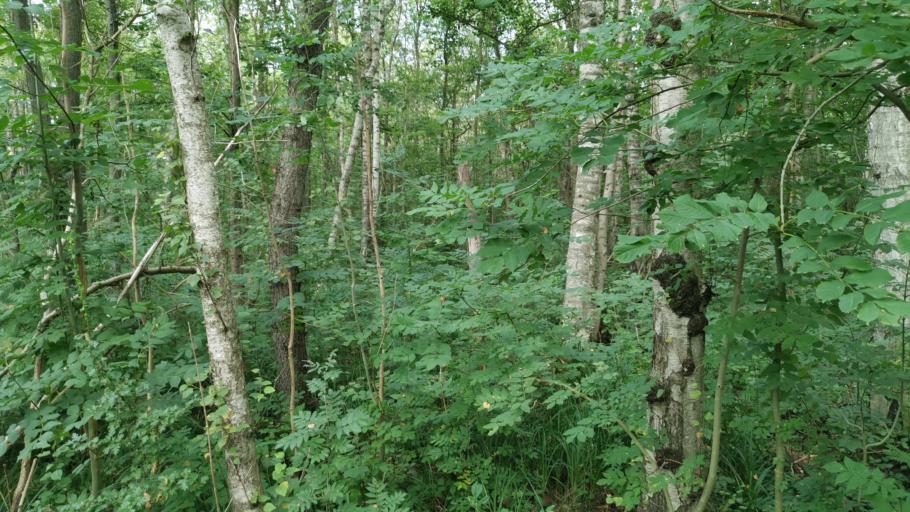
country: DE
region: Mecklenburg-Vorpommern
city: Zarrentin
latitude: 53.5447
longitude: 10.9325
